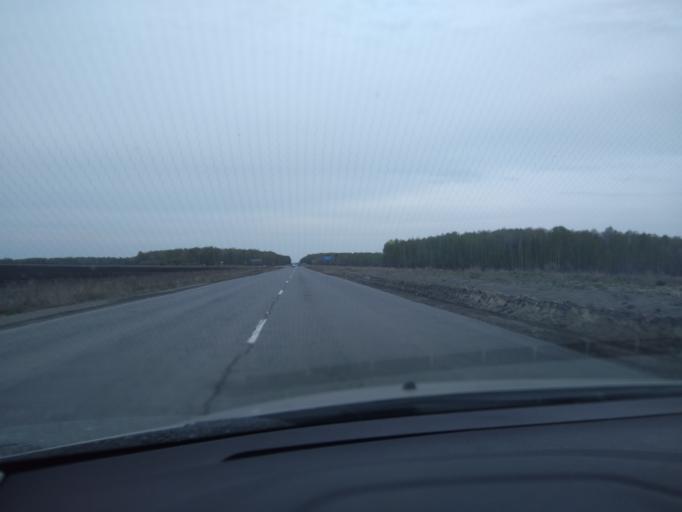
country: RU
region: Sverdlovsk
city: Kamyshlov
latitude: 56.8785
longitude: 62.9772
